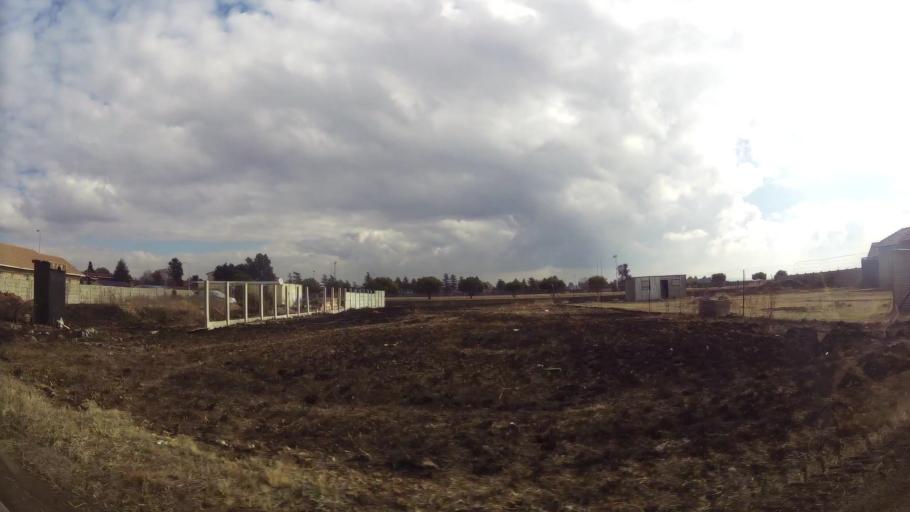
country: ZA
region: Gauteng
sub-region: Sedibeng District Municipality
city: Meyerton
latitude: -26.6020
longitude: 28.0492
